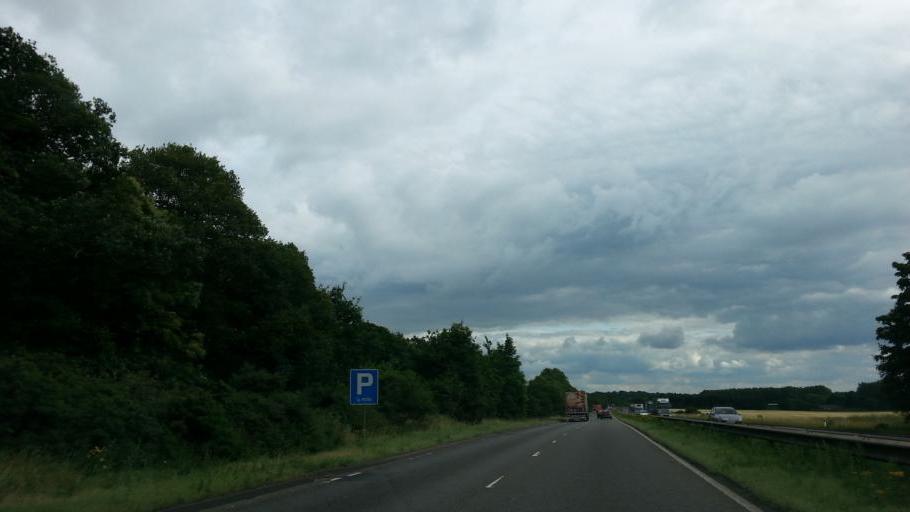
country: GB
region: England
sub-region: Nottinghamshire
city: Babworth
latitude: 53.3337
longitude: -1.0281
